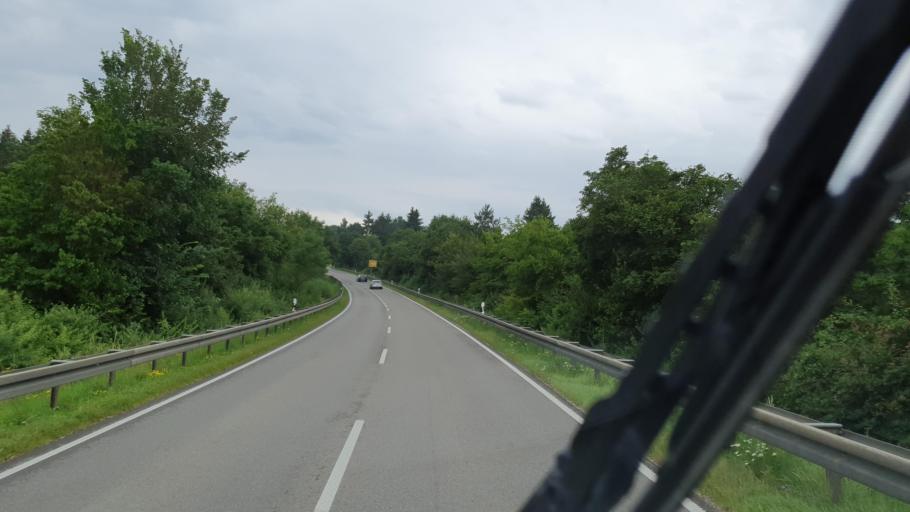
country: DE
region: Baden-Wuerttemberg
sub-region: Tuebingen Region
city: Berghulen
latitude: 48.4806
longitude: 9.7453
